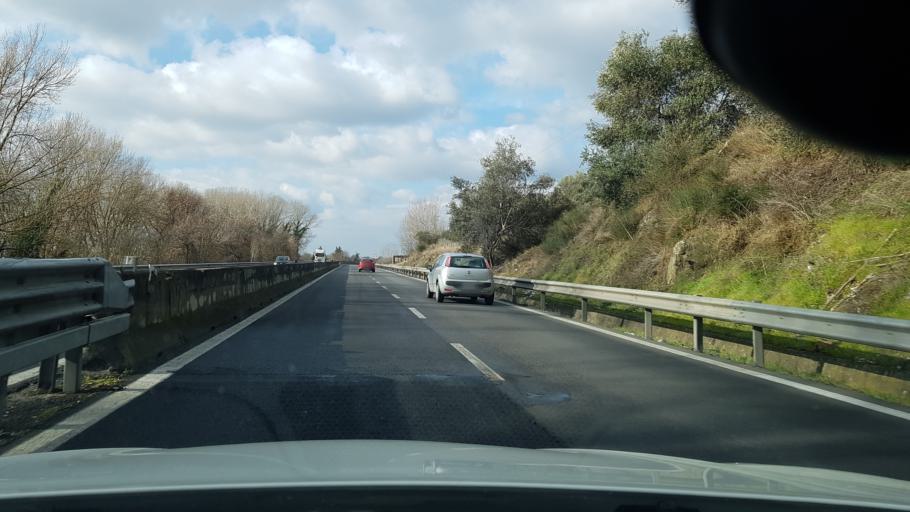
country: IT
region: Tuscany
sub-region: Province of Arezzo
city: Terontola
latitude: 43.1873
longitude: 12.0406
